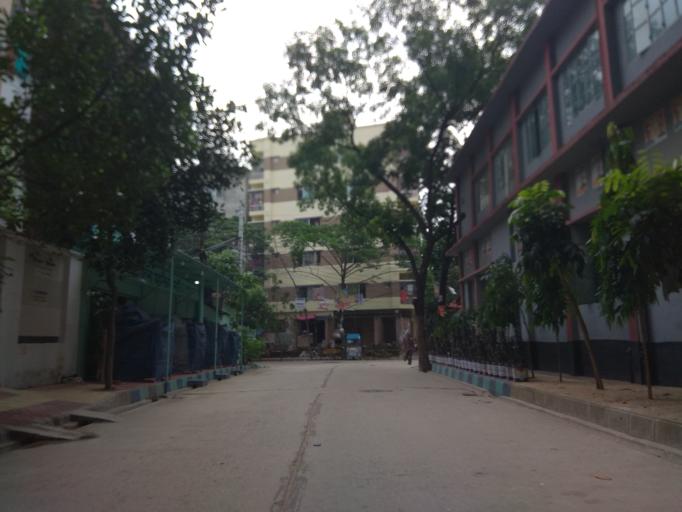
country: BD
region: Dhaka
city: Azimpur
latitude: 23.8091
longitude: 90.3639
